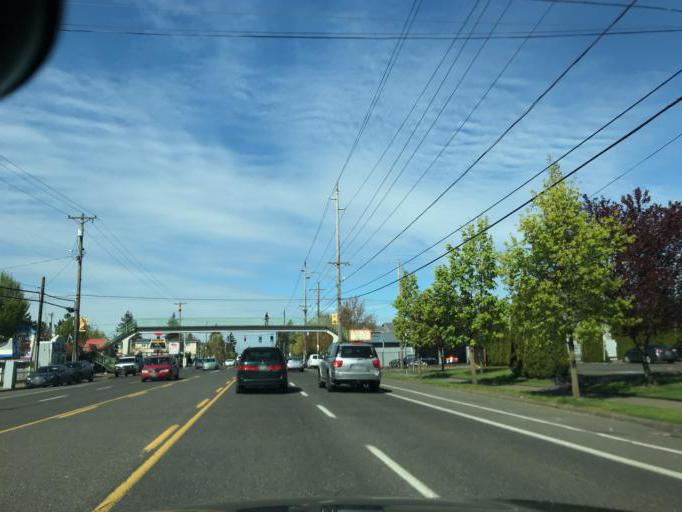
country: US
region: Oregon
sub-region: Multnomah County
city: Lents
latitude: 45.5041
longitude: -122.5220
